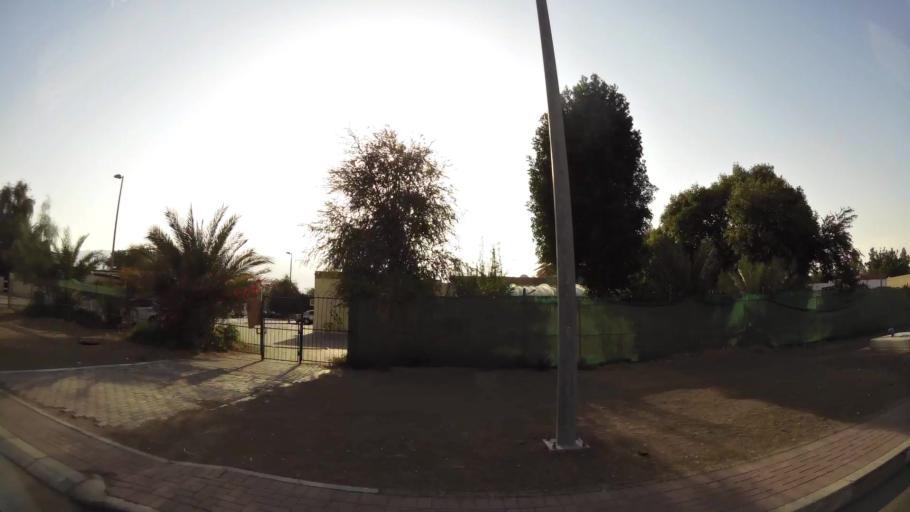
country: AE
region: Abu Dhabi
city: Al Ain
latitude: 24.0850
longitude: 55.8389
